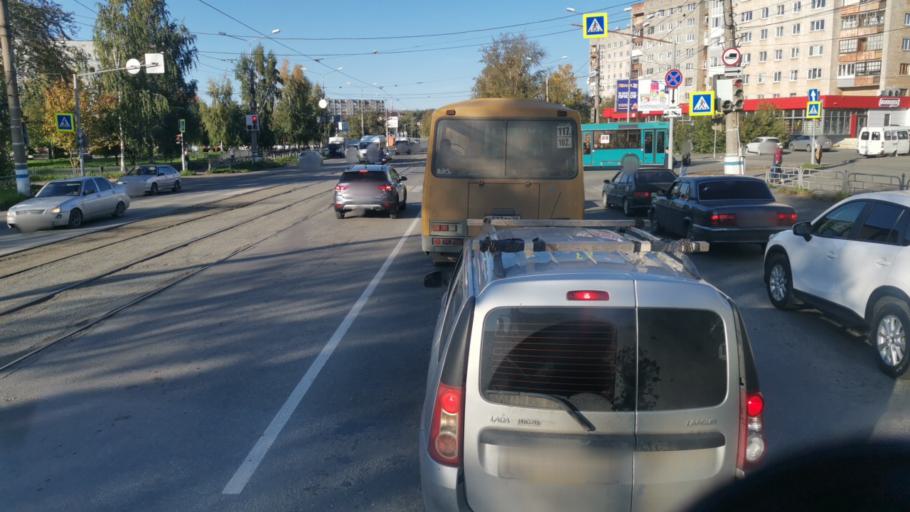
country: RU
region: Sverdlovsk
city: Nizhniy Tagil
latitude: 57.9103
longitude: 59.9472
